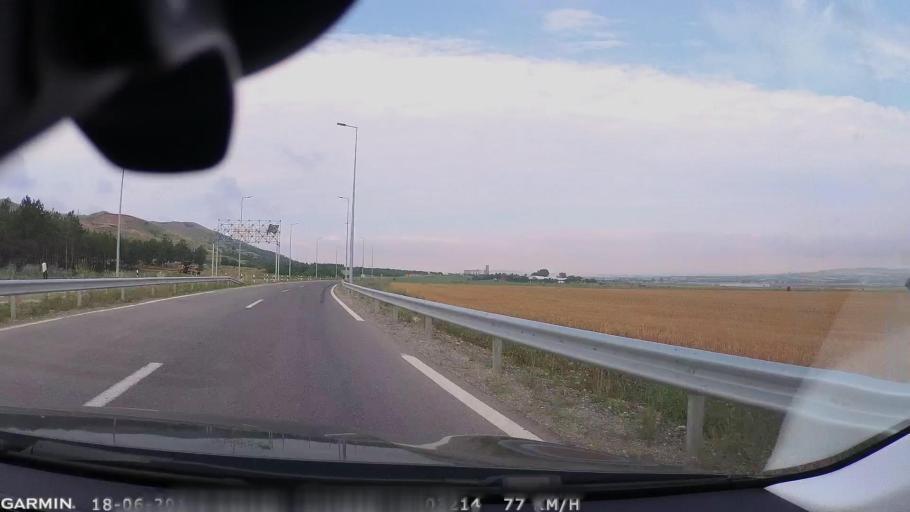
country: MK
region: Sveti Nikole
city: Sveti Nikole
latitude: 41.8102
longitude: 22.0308
